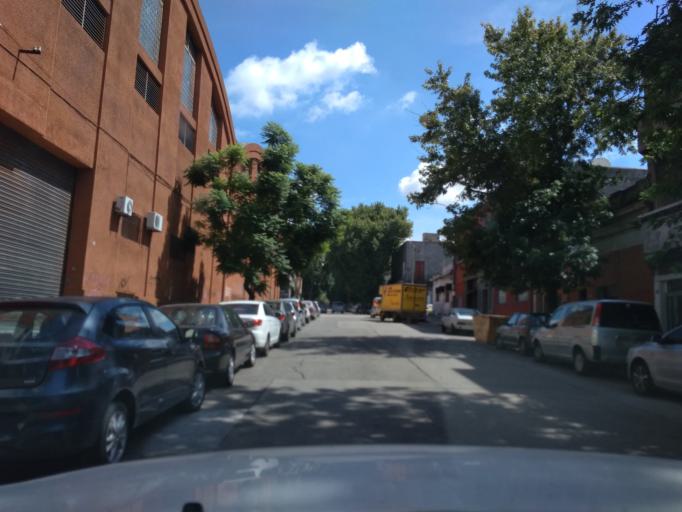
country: UY
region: Montevideo
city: Montevideo
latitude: -34.8817
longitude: -56.1965
